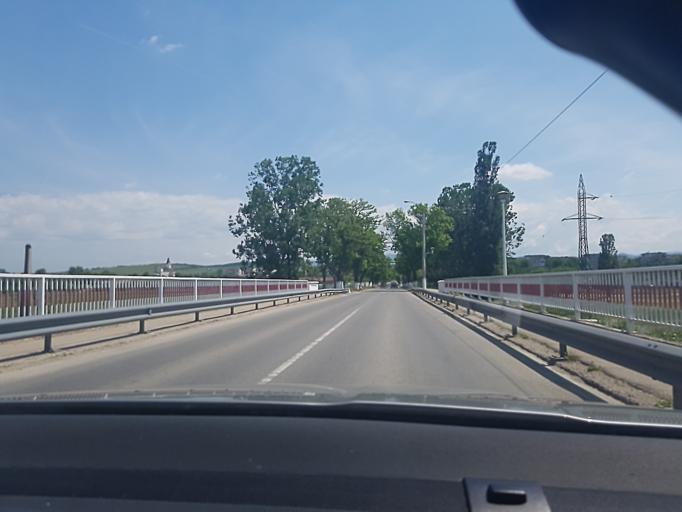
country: RO
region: Hunedoara
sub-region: Comuna Calan
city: Calan
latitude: 45.7344
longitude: 23.0151
